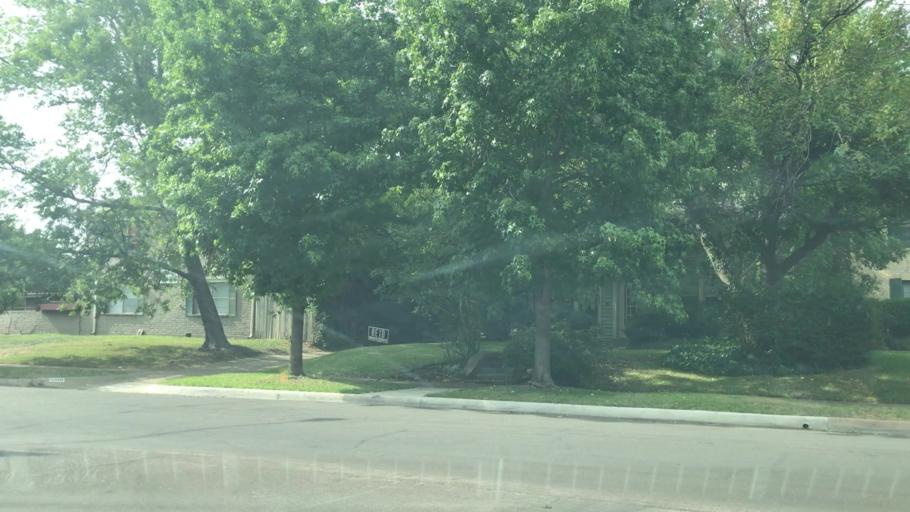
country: US
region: Texas
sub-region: Dallas County
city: Highland Park
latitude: 32.8067
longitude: -96.7650
